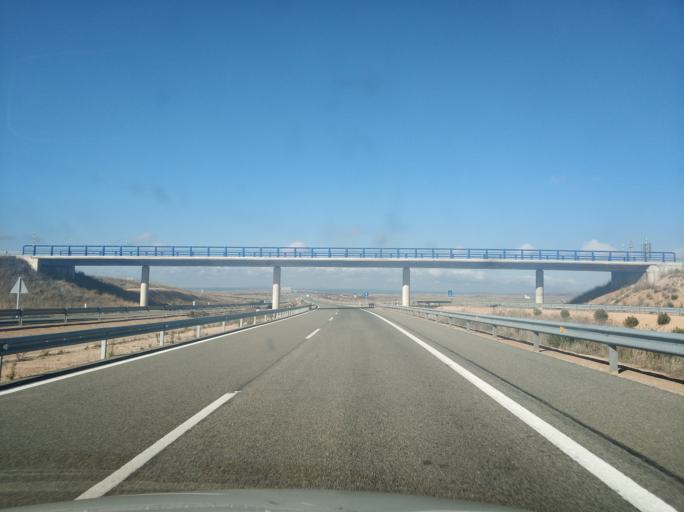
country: ES
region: Castille and Leon
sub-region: Provincia de Soria
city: Adradas
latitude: 41.3840
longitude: -2.4668
